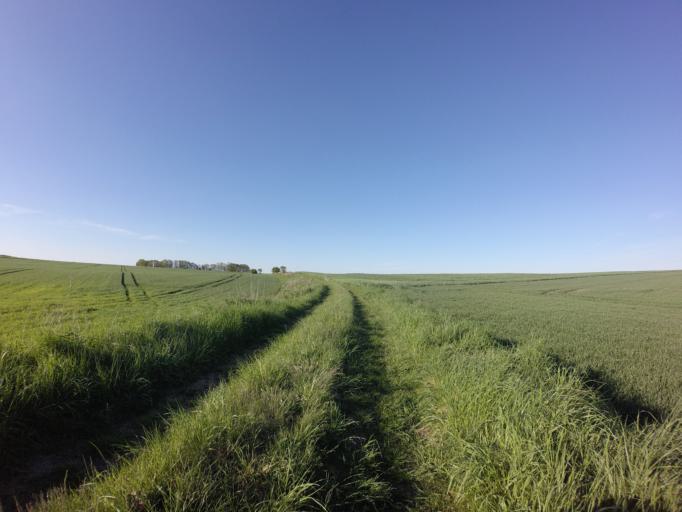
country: PL
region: West Pomeranian Voivodeship
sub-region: Powiat choszczenski
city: Choszczno
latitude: 53.1489
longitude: 15.3678
